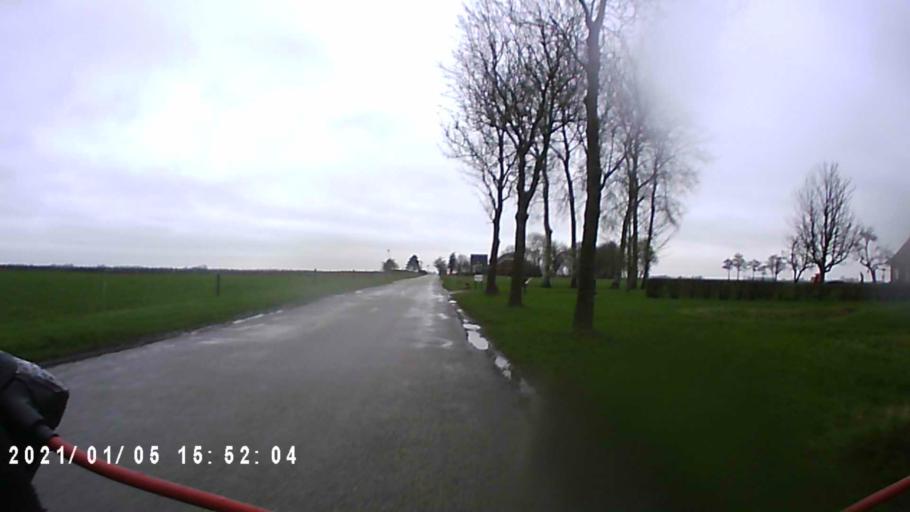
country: NL
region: Groningen
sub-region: Gemeente  Oldambt
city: Winschoten
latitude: 53.2012
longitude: 7.1005
